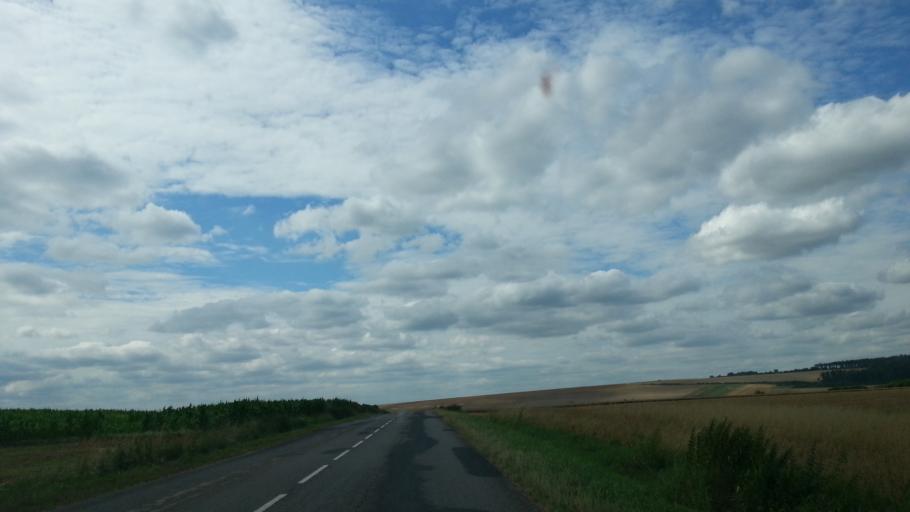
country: FR
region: Lorraine
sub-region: Departement de la Meuse
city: Belleville-sur-Meuse
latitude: 49.2092
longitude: 5.3496
